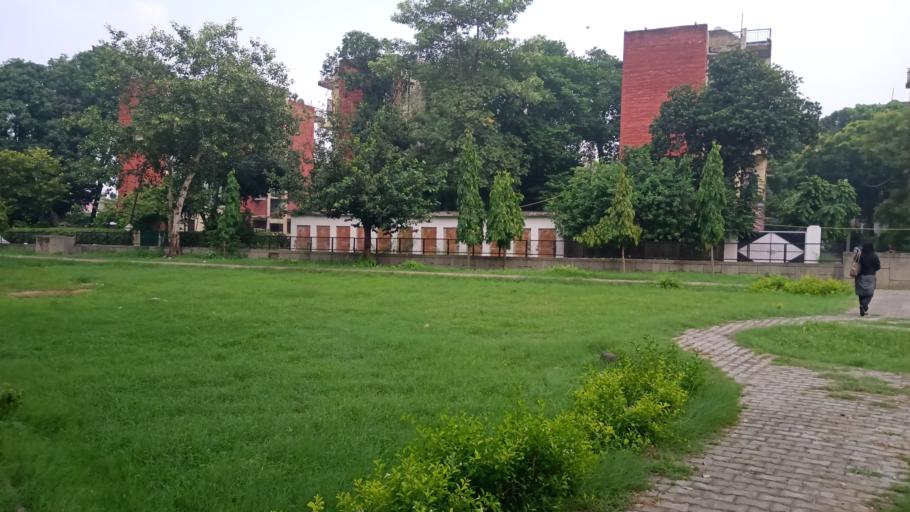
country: IN
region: NCT
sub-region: New Delhi
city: New Delhi
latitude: 28.5753
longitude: 77.2499
